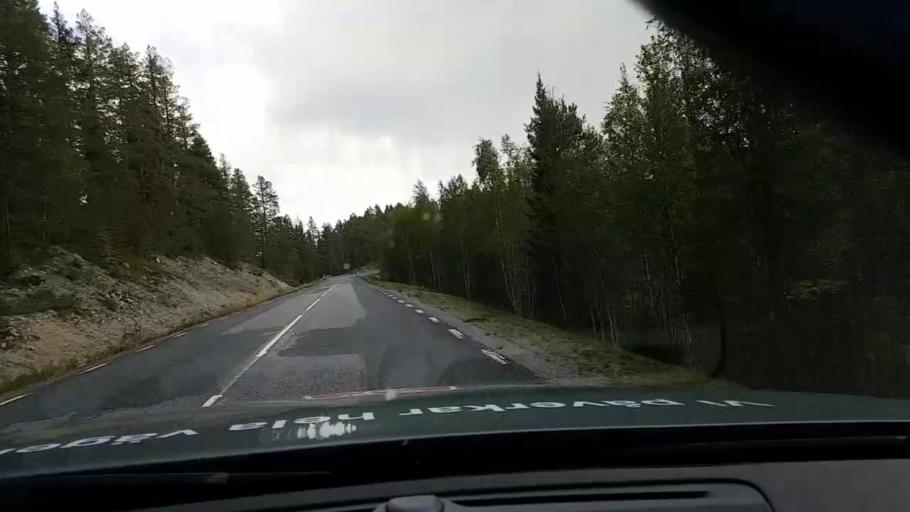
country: SE
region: Vaesterbotten
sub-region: Asele Kommun
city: Asele
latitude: 63.8395
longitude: 17.4314
